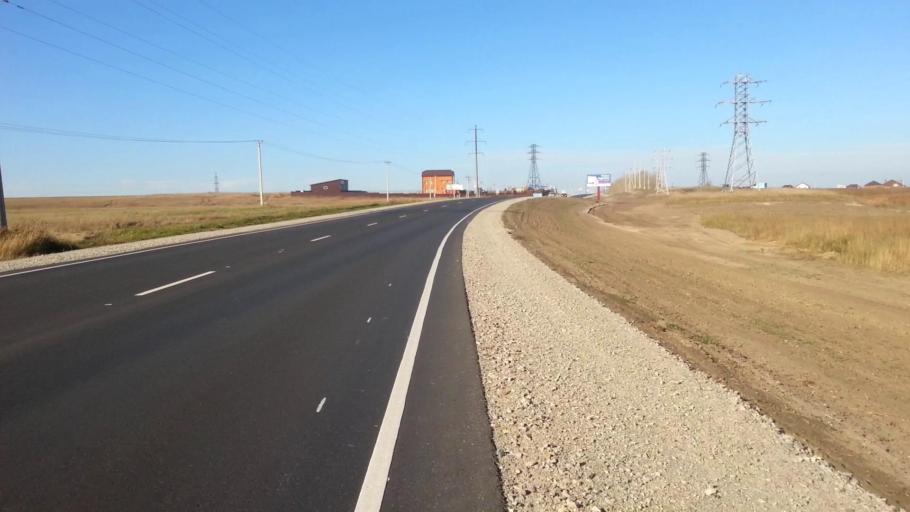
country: RU
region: Altai Krai
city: Sannikovo
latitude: 53.3328
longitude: 83.9381
